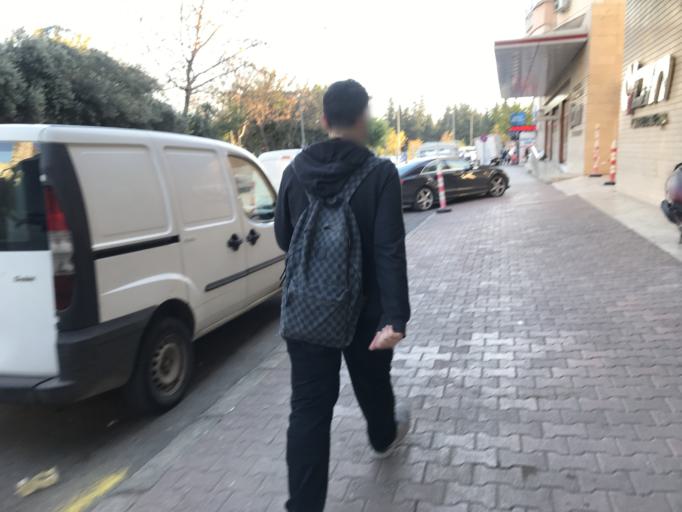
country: TR
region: Antalya
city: Antalya
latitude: 36.8965
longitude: 30.7072
